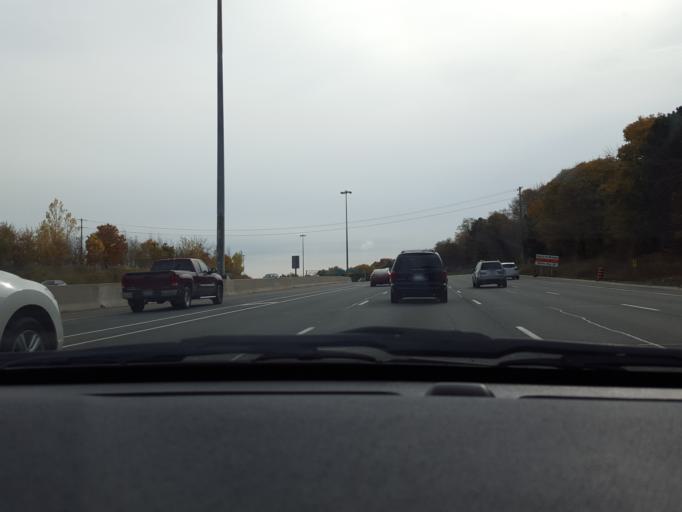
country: CA
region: Ontario
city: Willowdale
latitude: 43.8195
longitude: -79.3606
